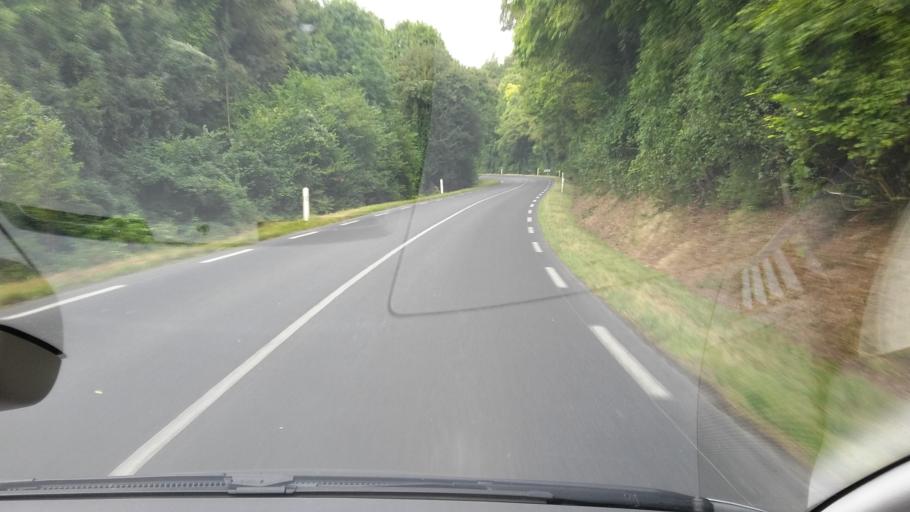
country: FR
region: Champagne-Ardenne
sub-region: Departement de la Marne
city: Verzenay
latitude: 49.1301
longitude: 4.1055
